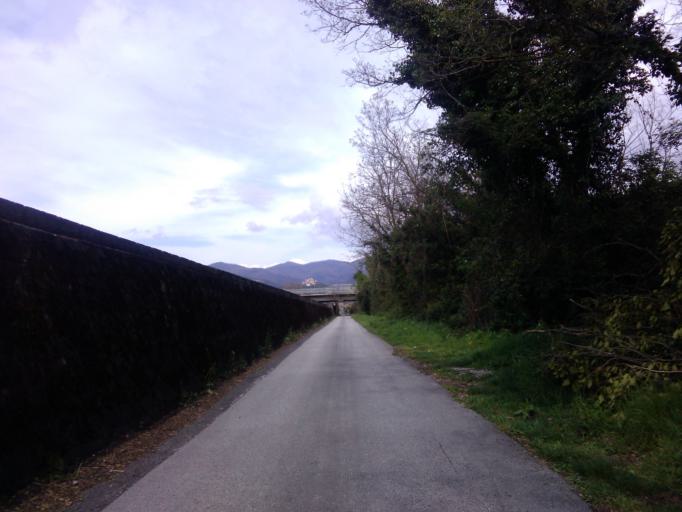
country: IT
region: Tuscany
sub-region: Provincia di Massa-Carrara
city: Marina di Carrara
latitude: 44.0538
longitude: 10.0251
